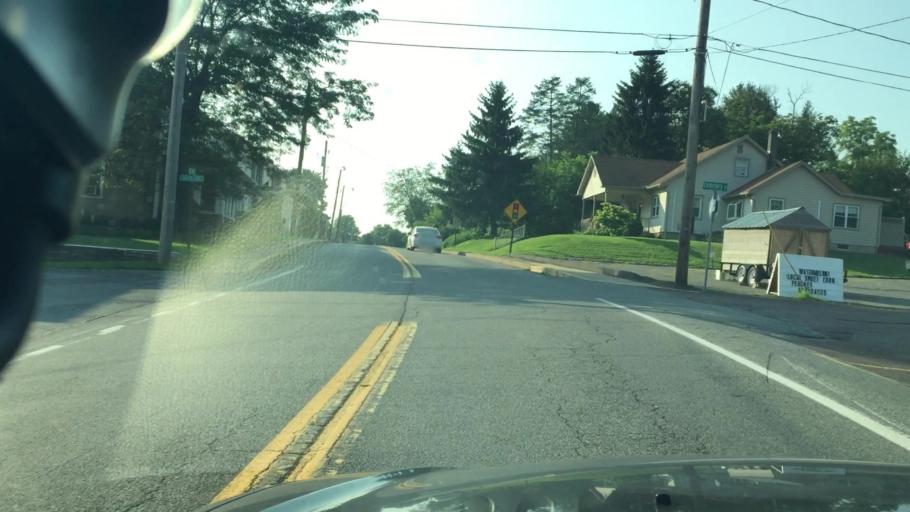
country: US
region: Pennsylvania
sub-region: Columbia County
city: Catawissa
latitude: 40.9485
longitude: -76.4568
